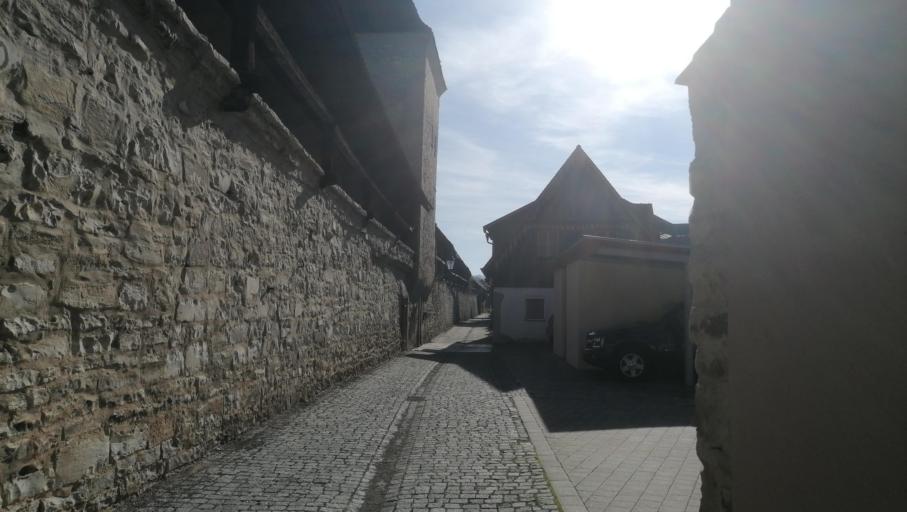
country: DE
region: Bavaria
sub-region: Upper Palatinate
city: Berching
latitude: 49.1079
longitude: 11.4407
